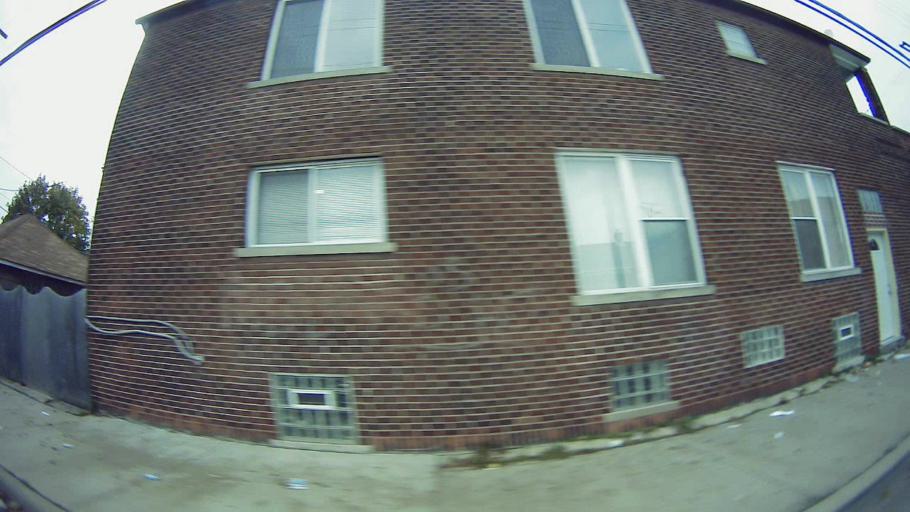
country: US
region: Michigan
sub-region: Wayne County
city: Hamtramck
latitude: 42.4001
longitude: -83.0632
